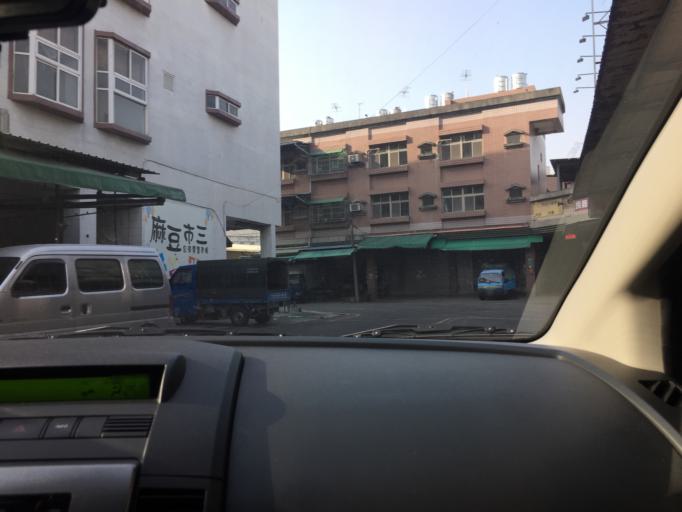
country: TW
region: Taiwan
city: Xinying
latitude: 23.1853
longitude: 120.2497
